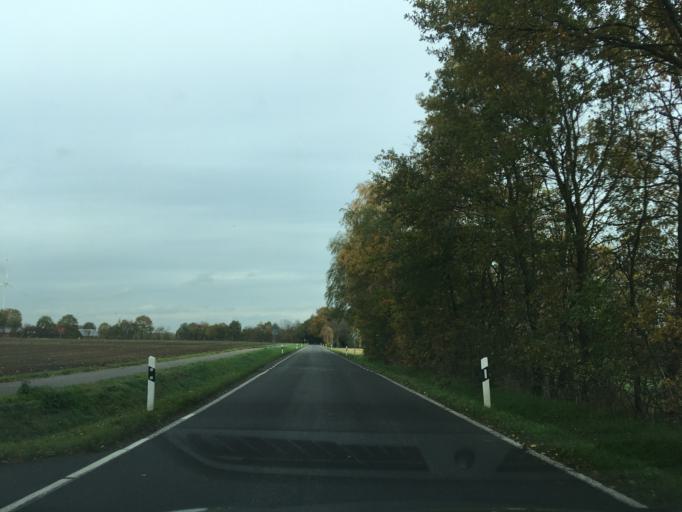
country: DE
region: North Rhine-Westphalia
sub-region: Regierungsbezirk Munster
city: Vreden
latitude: 52.0477
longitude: 6.8595
